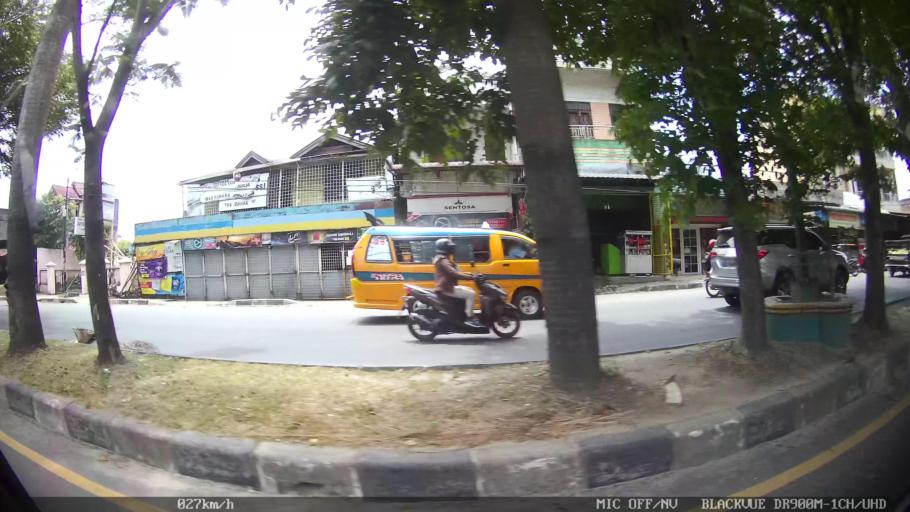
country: ID
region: North Sumatra
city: Deli Tua
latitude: 3.5338
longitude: 98.6481
